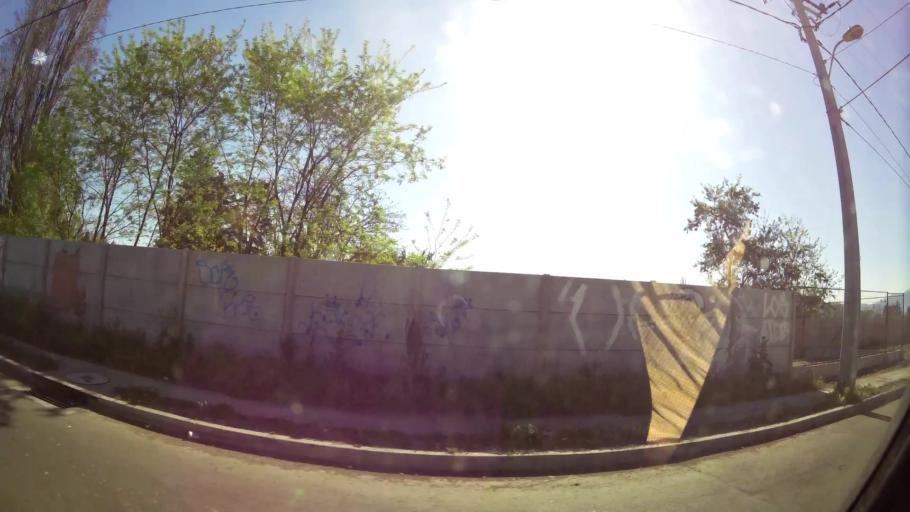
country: CL
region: Santiago Metropolitan
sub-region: Provincia de Talagante
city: Penaflor
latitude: -33.6156
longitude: -70.8810
